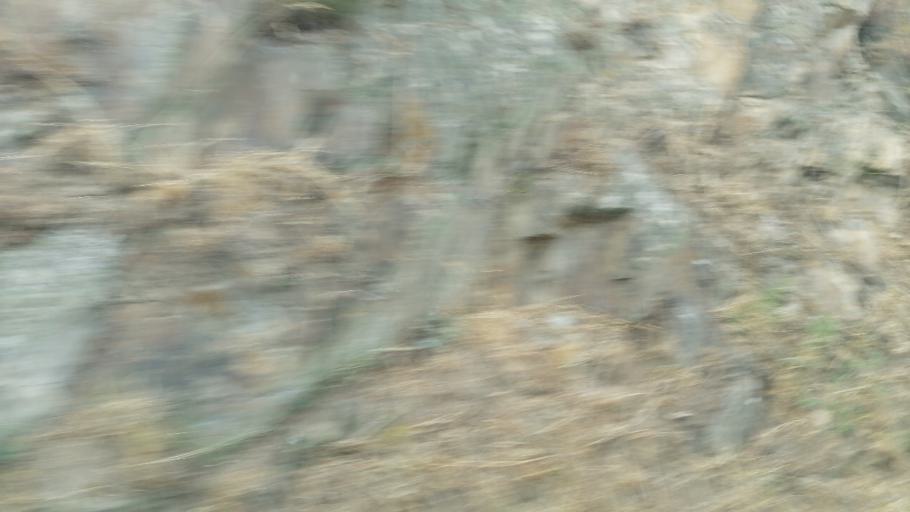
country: PT
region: Viseu
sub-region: Sao Joao da Pesqueira
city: Sao Joao da Pesqueira
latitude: 41.0785
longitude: -7.3886
